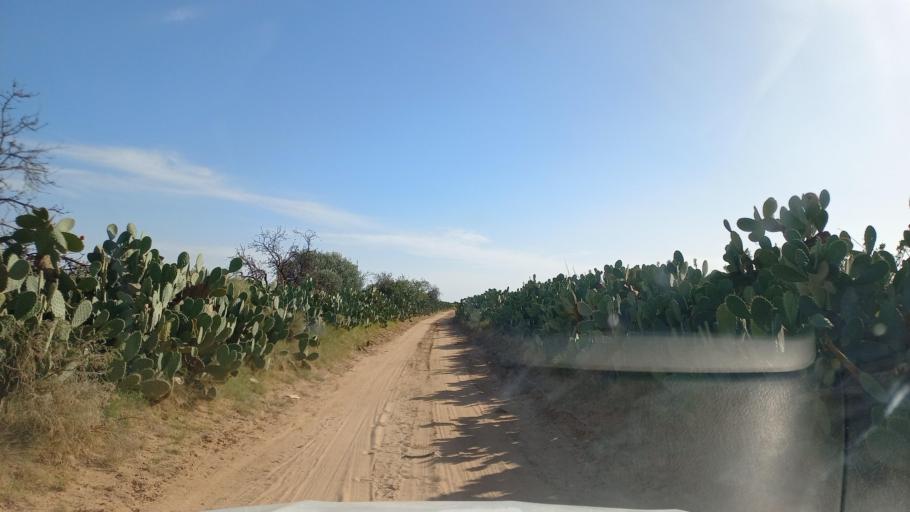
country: TN
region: Al Qasrayn
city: Sbiba
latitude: 35.3331
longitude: 9.1253
